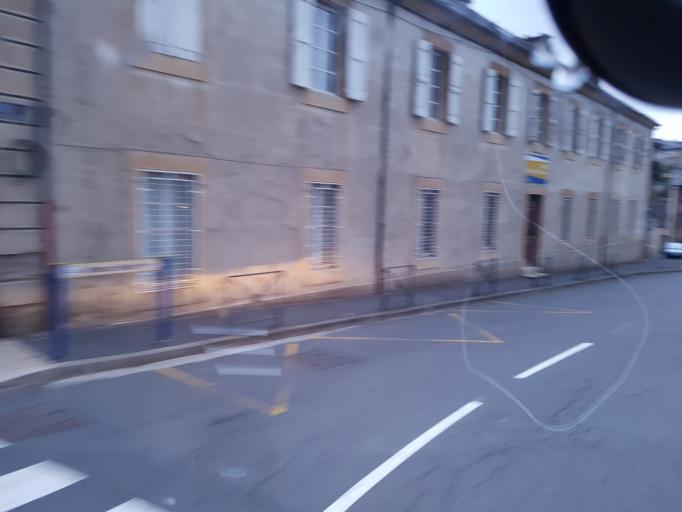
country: FR
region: Languedoc-Roussillon
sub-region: Departement de la Lozere
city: Mende
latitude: 44.5197
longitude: 3.4971
